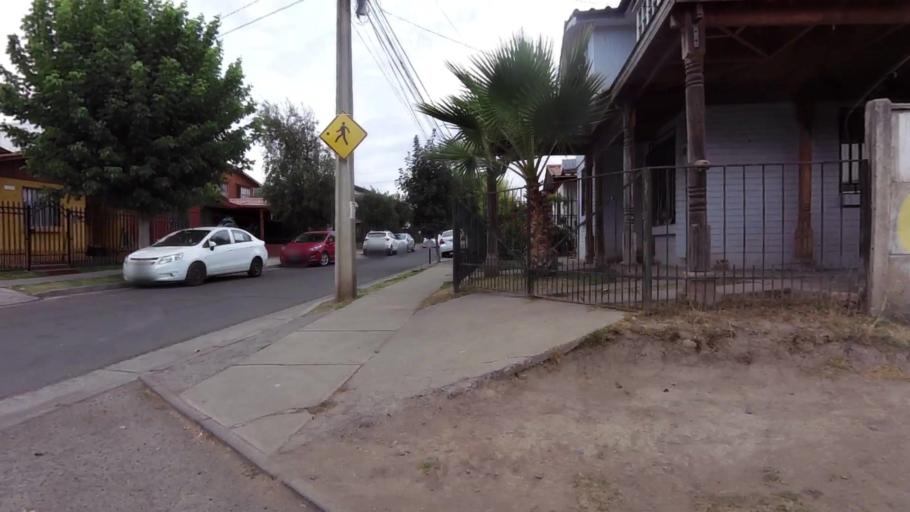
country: CL
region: O'Higgins
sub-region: Provincia de Cachapoal
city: Rancagua
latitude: -34.1400
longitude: -70.7362
